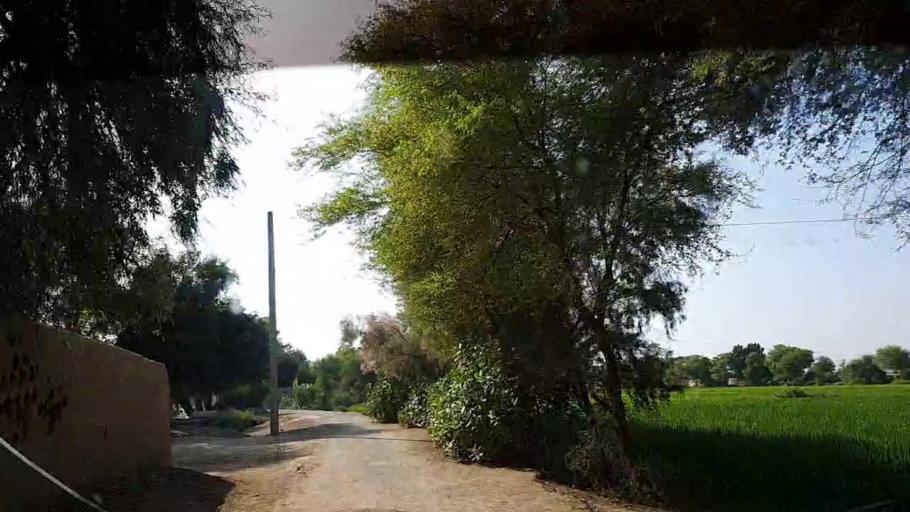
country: PK
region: Sindh
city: Tangwani
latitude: 28.2390
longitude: 68.9928
